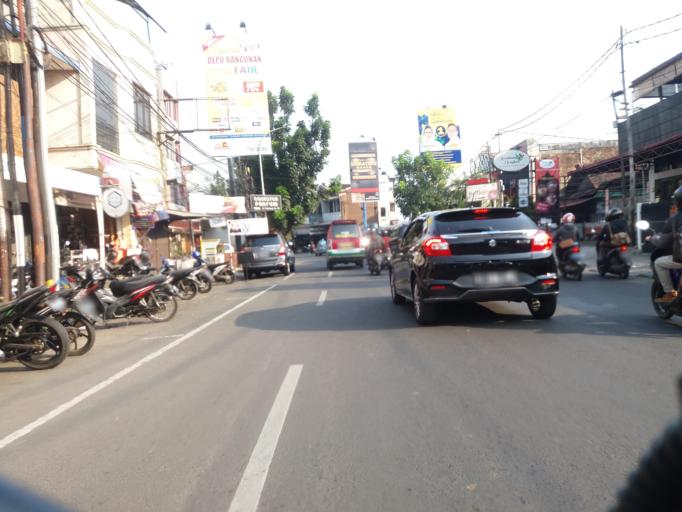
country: ID
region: West Java
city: Bandung
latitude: -6.9244
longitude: 107.6117
